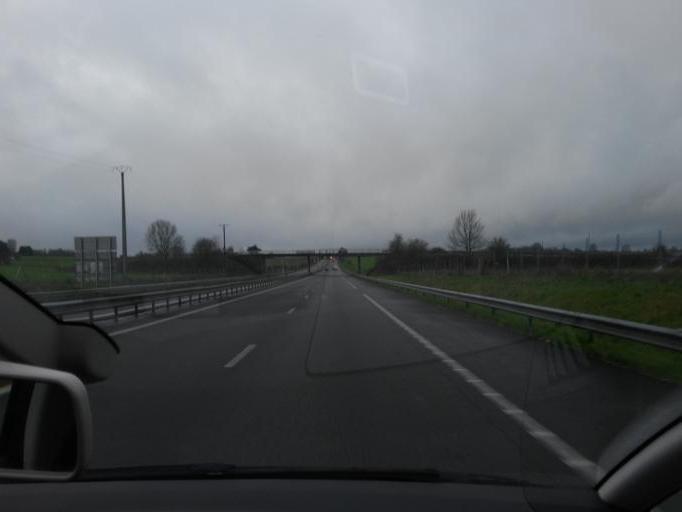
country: FR
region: Nord-Pas-de-Calais
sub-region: Departement du Pas-de-Calais
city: Hermies
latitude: 50.1191
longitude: 3.0837
